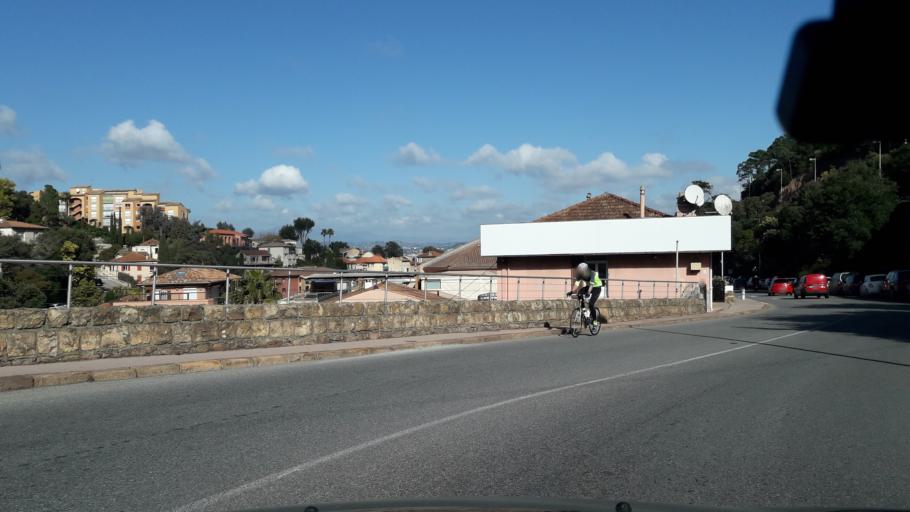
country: FR
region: Provence-Alpes-Cote d'Azur
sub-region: Departement des Alpes-Maritimes
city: Theoule-sur-Mer
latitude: 43.5043
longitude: 6.9386
